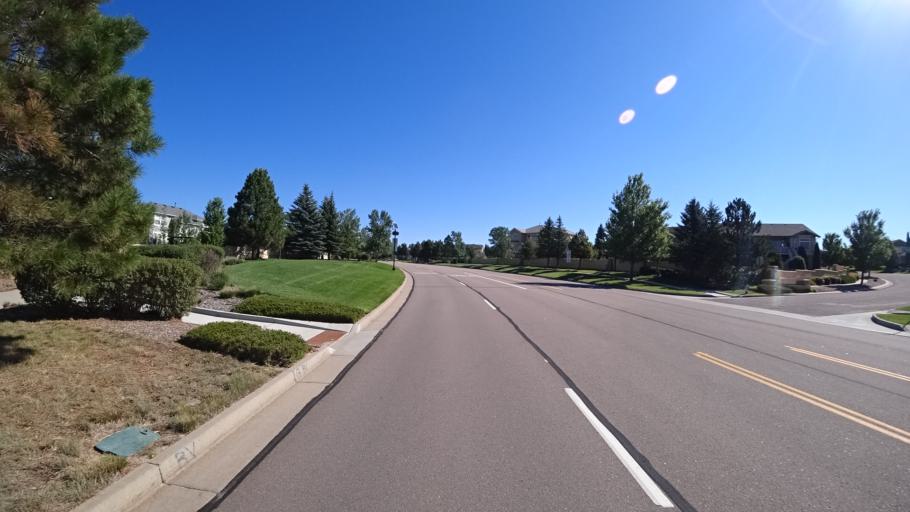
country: US
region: Colorado
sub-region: El Paso County
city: Black Forest
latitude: 38.9770
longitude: -104.7710
